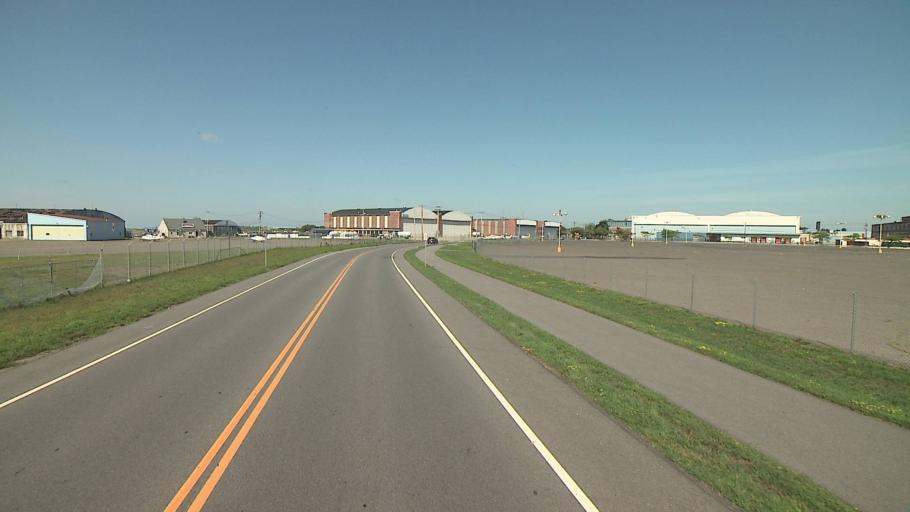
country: US
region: Connecticut
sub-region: Fairfield County
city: Stratford
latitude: 41.1672
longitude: -73.1208
